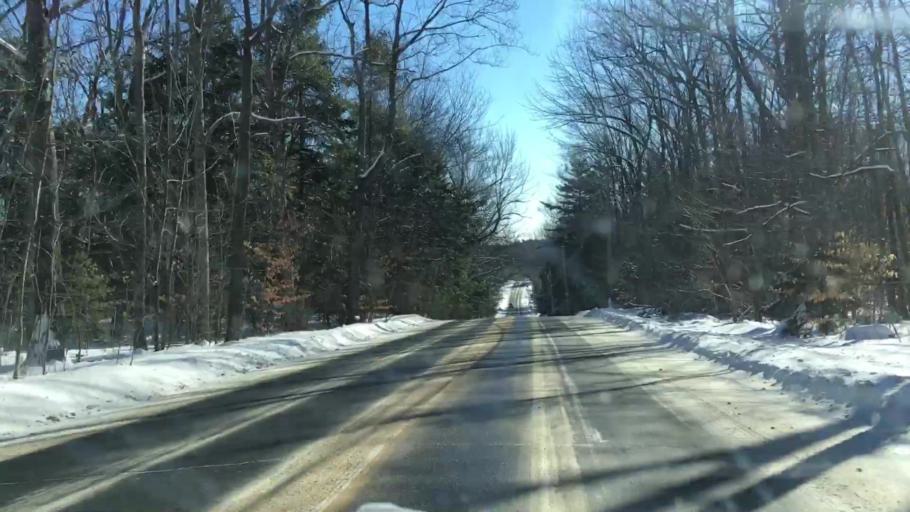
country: US
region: Maine
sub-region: Androscoggin County
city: Lisbon Falls
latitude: 43.9380
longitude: -70.0655
